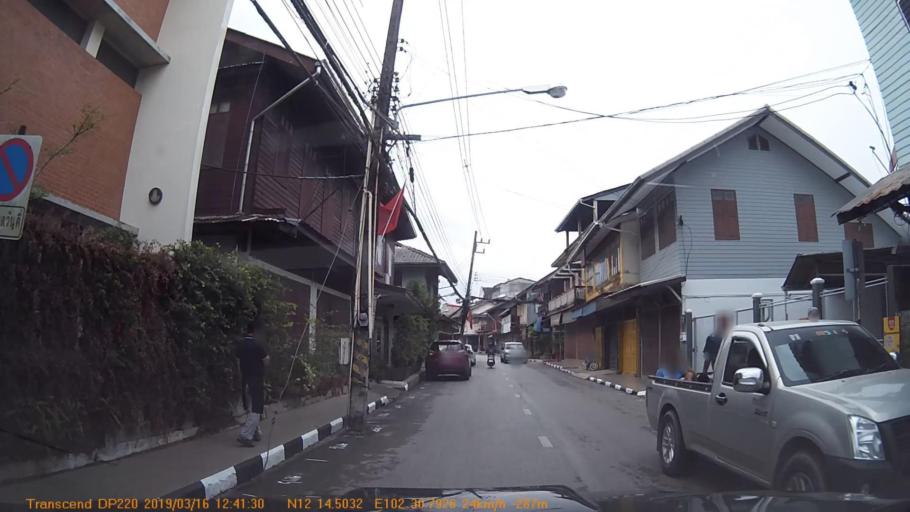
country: TH
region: Trat
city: Trat
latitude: 12.2418
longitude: 102.5131
